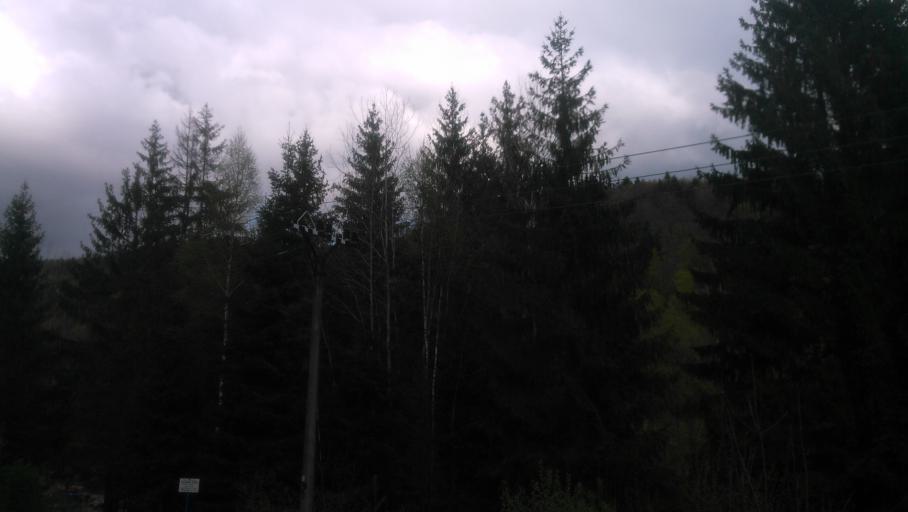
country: SK
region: Banskobystricky
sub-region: Okres Banska Bystrica
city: Brezno
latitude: 48.8644
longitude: 19.6040
